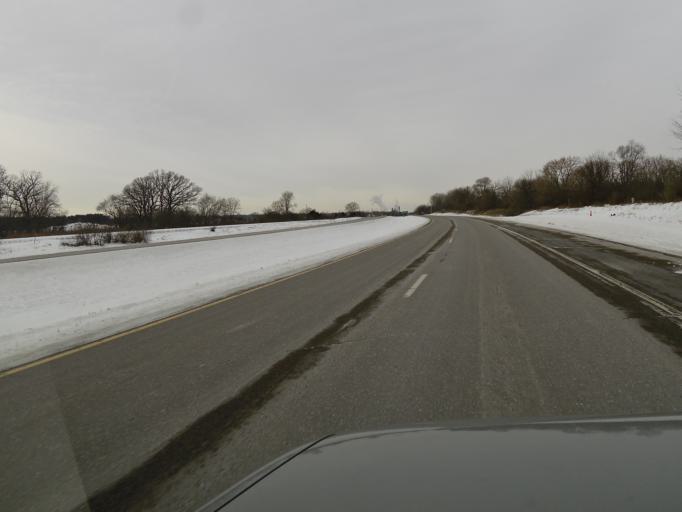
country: US
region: Minnesota
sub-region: Scott County
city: Shakopee
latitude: 44.8031
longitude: -93.4865
